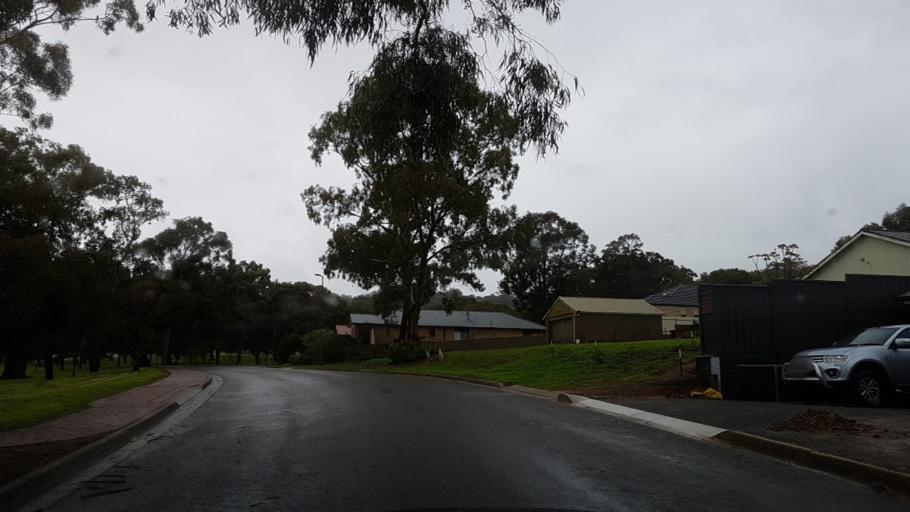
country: AU
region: South Australia
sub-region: Onkaparinga
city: Craigburn Farm
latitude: -35.0819
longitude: 138.5916
